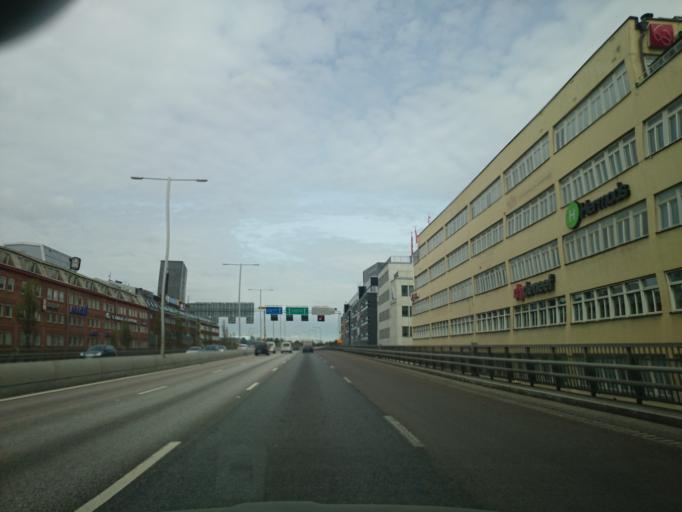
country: SE
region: Stockholm
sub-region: Solna Kommun
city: Solna
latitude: 59.3376
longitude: 18.0111
